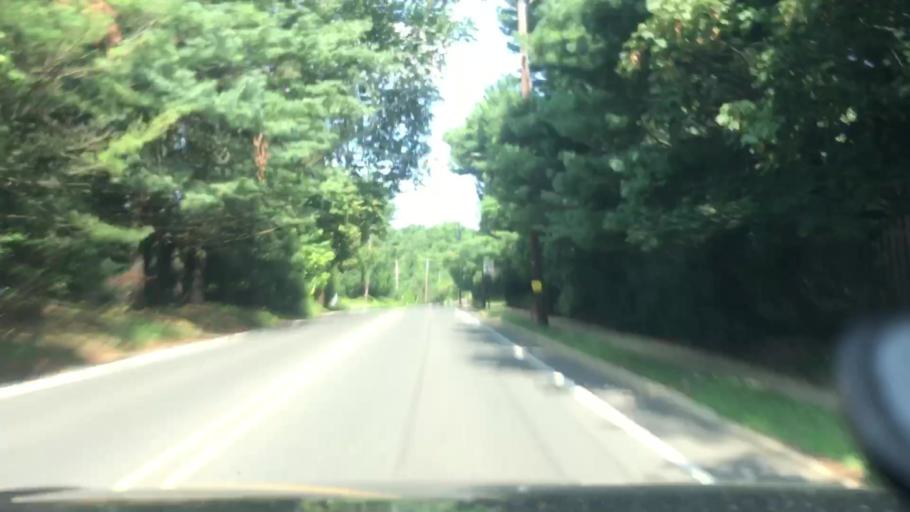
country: US
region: New Jersey
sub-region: Monmouth County
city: Little Silver
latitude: 40.3407
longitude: -74.0342
